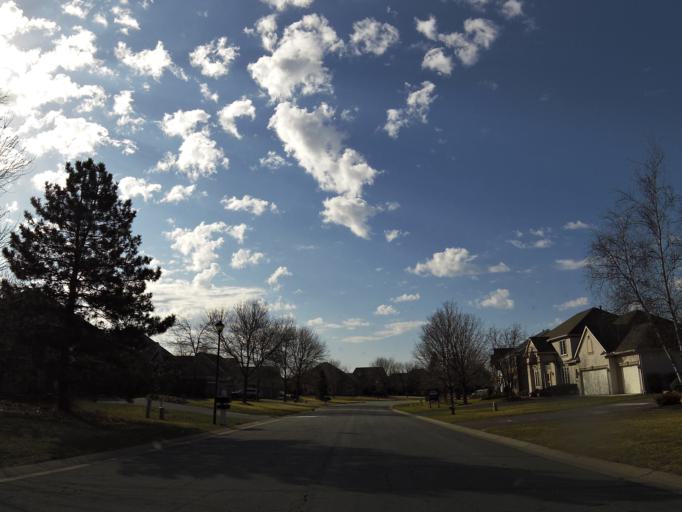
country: US
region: Minnesota
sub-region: Washington County
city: Woodbury
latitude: 44.8985
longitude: -92.8957
